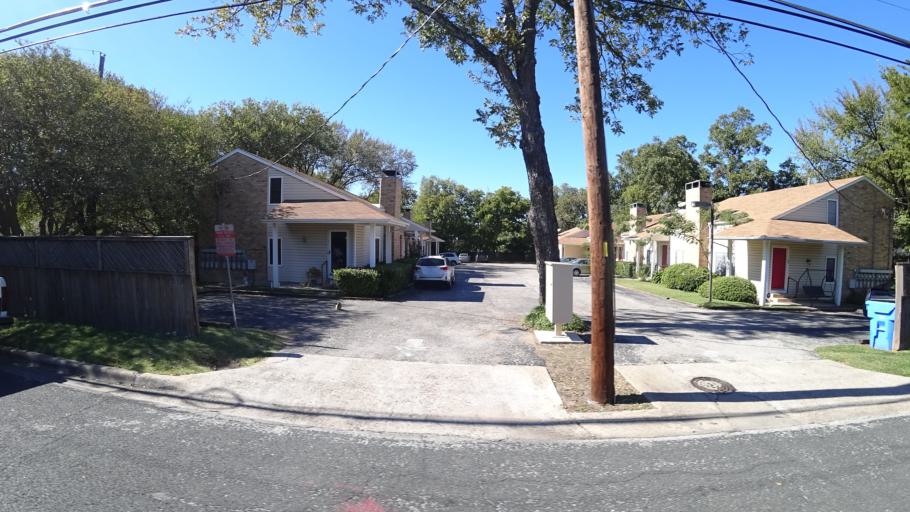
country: US
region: Texas
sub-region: Travis County
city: Austin
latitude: 30.3283
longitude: -97.7333
